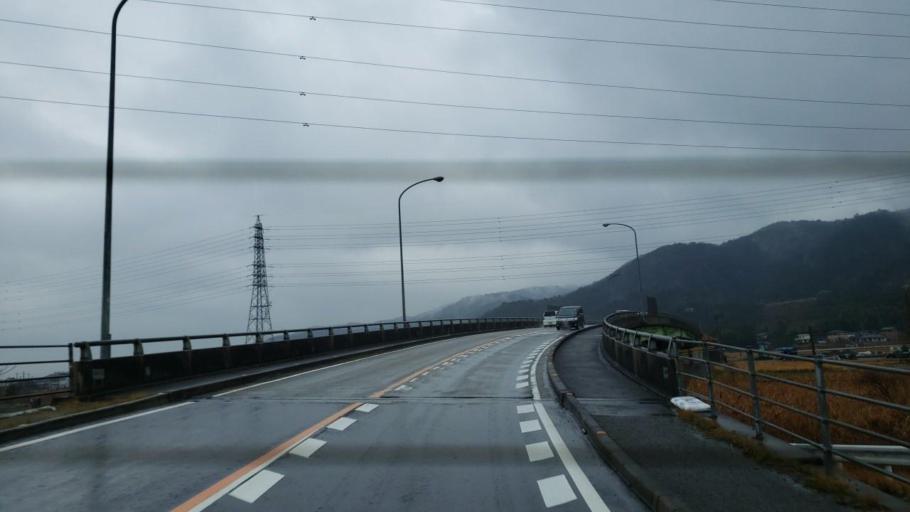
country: JP
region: Tokushima
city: Narutocho-mitsuishi
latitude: 34.1606
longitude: 134.5558
